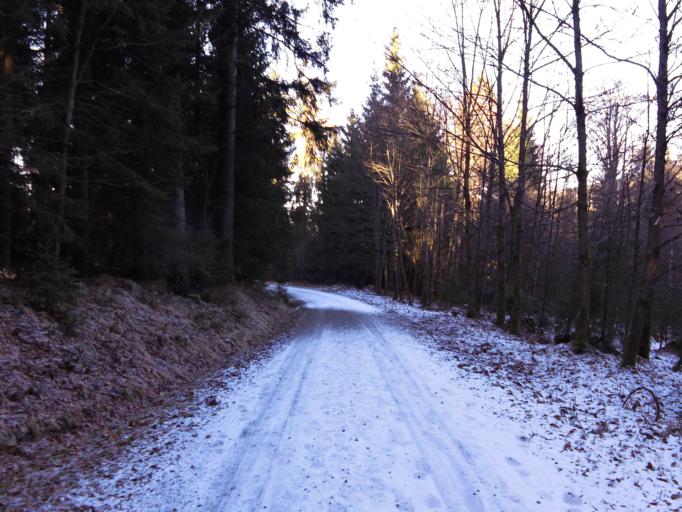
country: DE
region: Bavaria
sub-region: Upper Franconia
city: Fichtelberg
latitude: 50.0403
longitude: 11.8290
